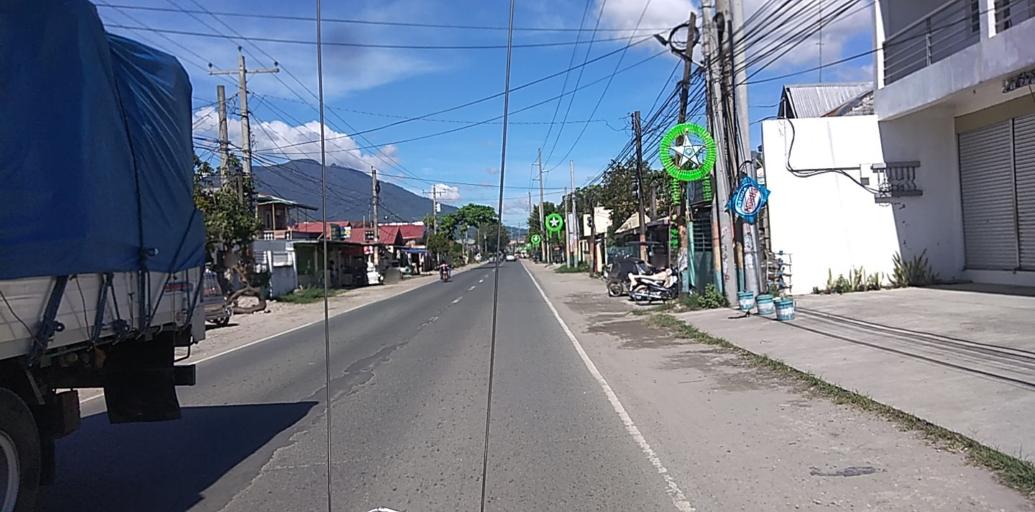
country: PH
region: Central Luzon
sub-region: Province of Pampanga
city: Arayat
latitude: 15.1311
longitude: 120.7749
